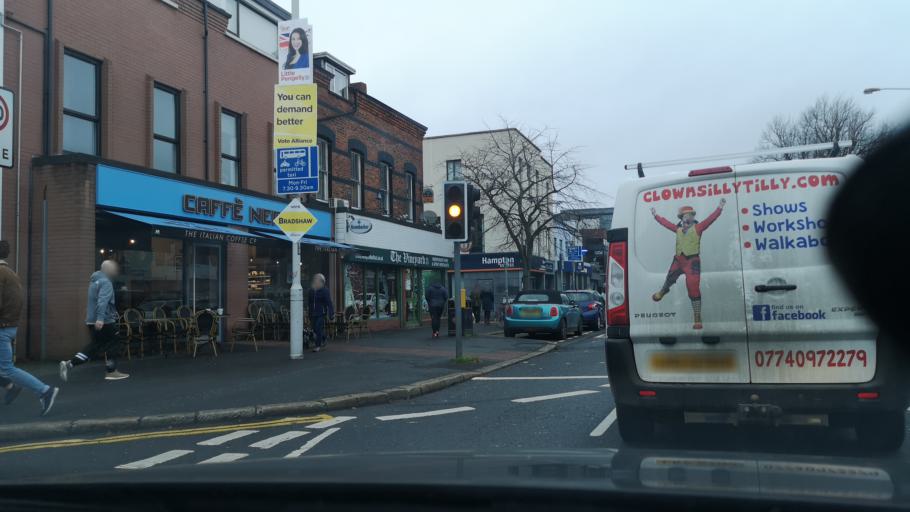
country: GB
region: Northern Ireland
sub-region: City of Belfast
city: Belfast
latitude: 54.5778
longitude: -5.9188
